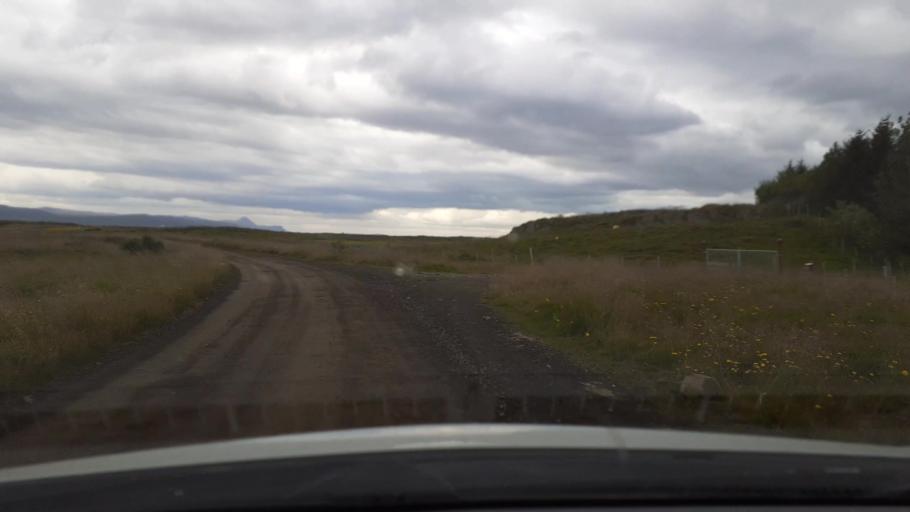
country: IS
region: West
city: Borgarnes
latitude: 64.6317
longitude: -21.9166
